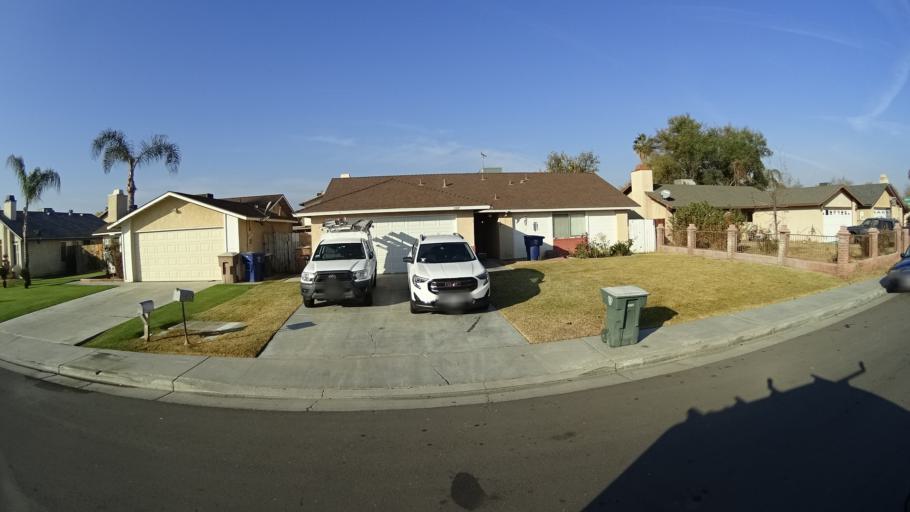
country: US
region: California
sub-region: Kern County
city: Greenfield
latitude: 35.3058
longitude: -119.0274
